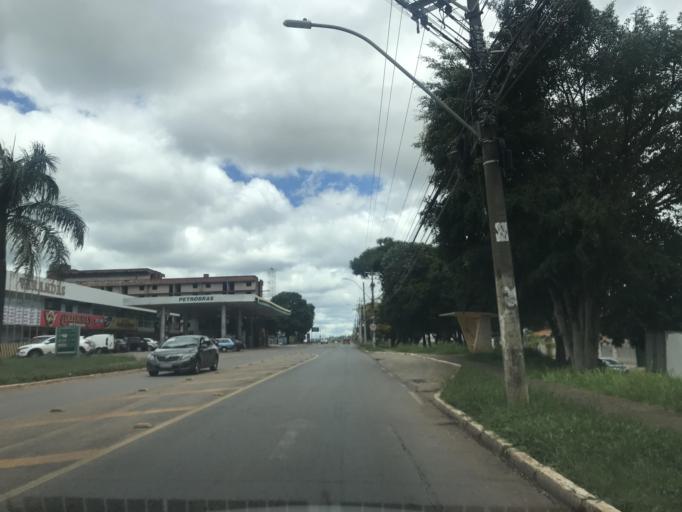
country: BR
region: Federal District
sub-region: Brasilia
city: Brasilia
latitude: -15.6521
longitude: -47.7891
